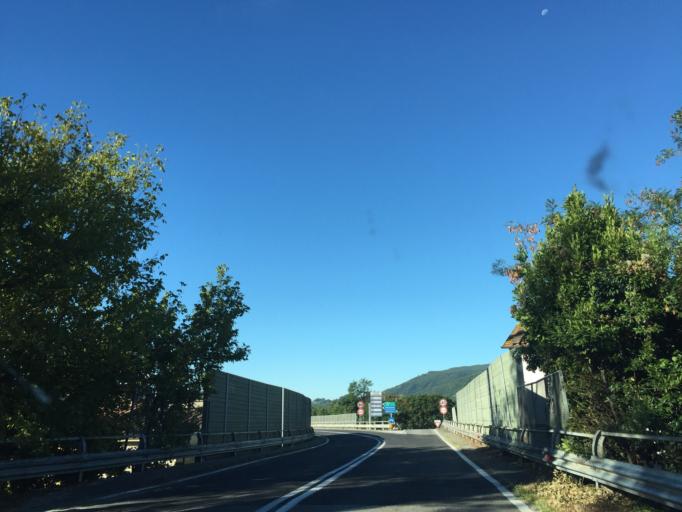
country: IT
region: Tuscany
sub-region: Provincia di Pistoia
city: Pistoia
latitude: 43.9577
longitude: 10.8998
